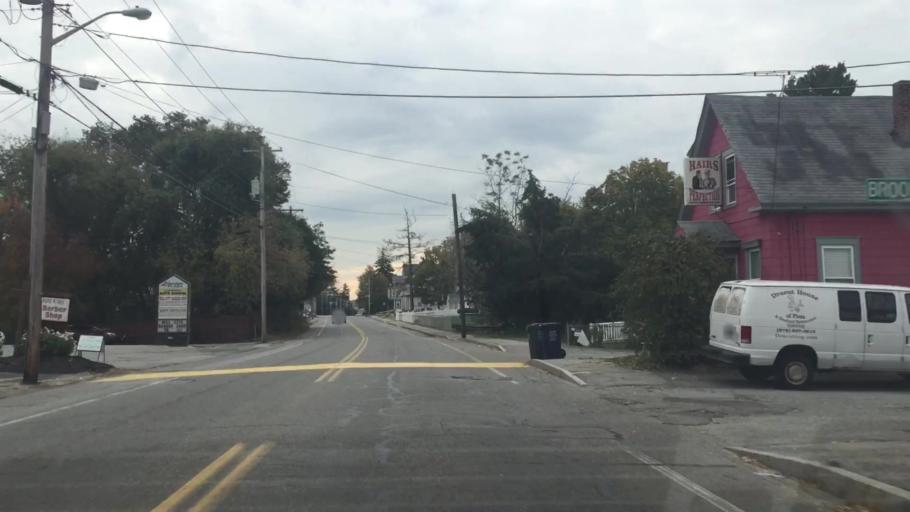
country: US
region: Massachusetts
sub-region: Middlesex County
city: Dracut
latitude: 42.6635
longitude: -71.3229
